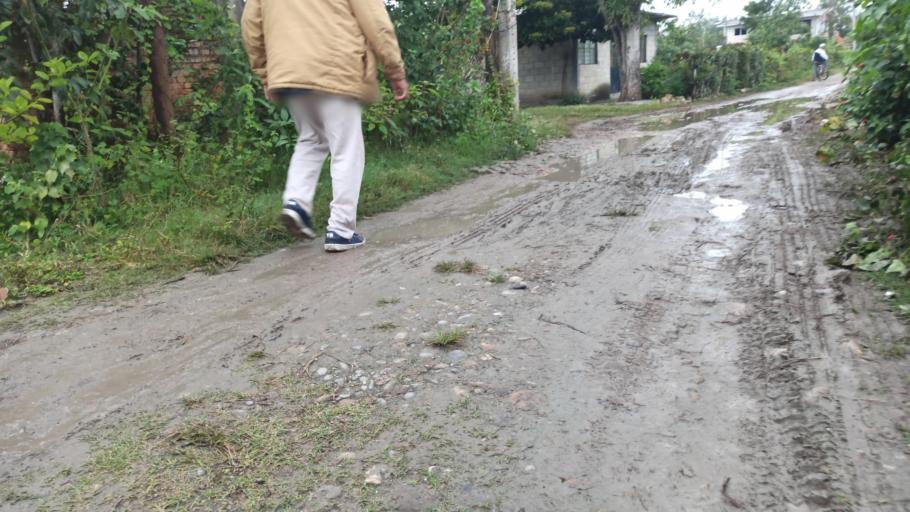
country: MX
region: Veracruz
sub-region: Papantla
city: El Chote
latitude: 20.3725
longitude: -97.3350
